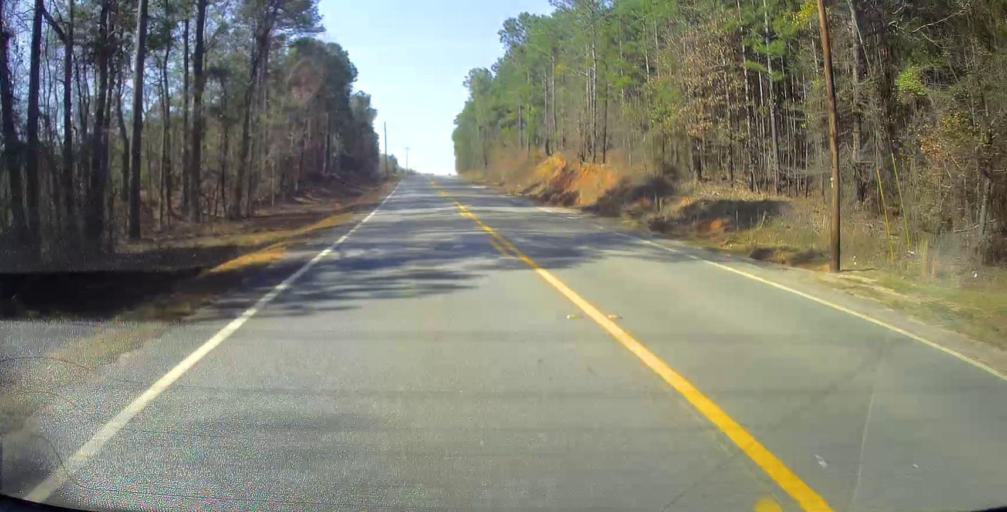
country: US
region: Georgia
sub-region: Wilkinson County
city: Gordon
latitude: 32.8439
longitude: -83.3366
